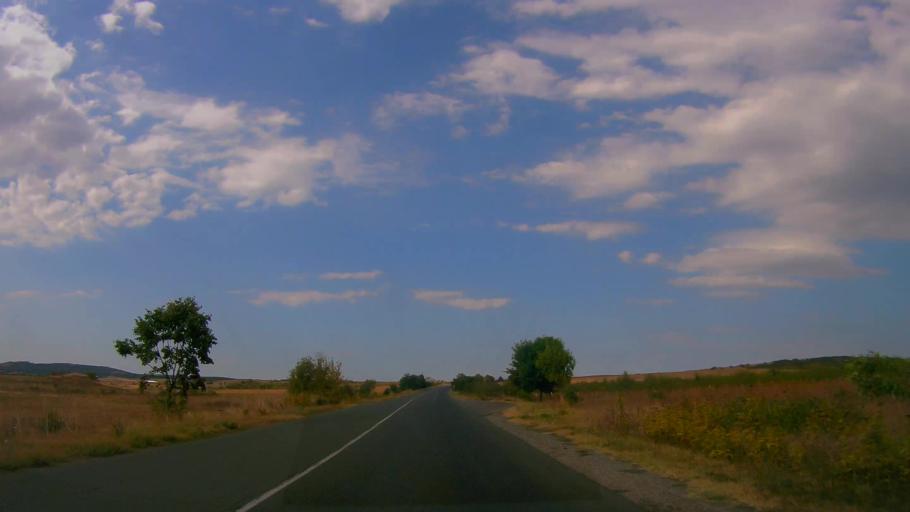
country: BG
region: Burgas
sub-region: Obshtina Aytos
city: Aytos
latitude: 42.6983
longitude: 27.2053
